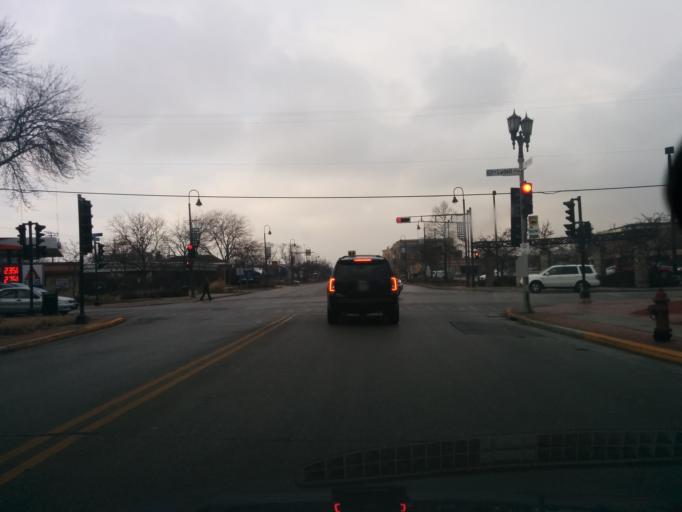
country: US
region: Wisconsin
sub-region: Milwaukee County
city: Whitefish Bay
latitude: 43.1186
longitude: -87.9112
